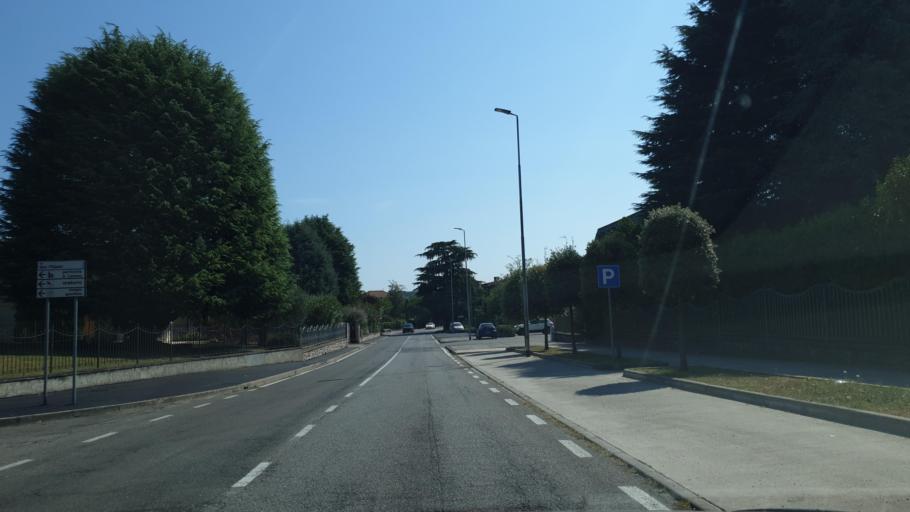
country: IT
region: Lombardy
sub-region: Provincia di Brescia
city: Carzago Riviera
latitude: 45.5261
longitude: 10.4550
